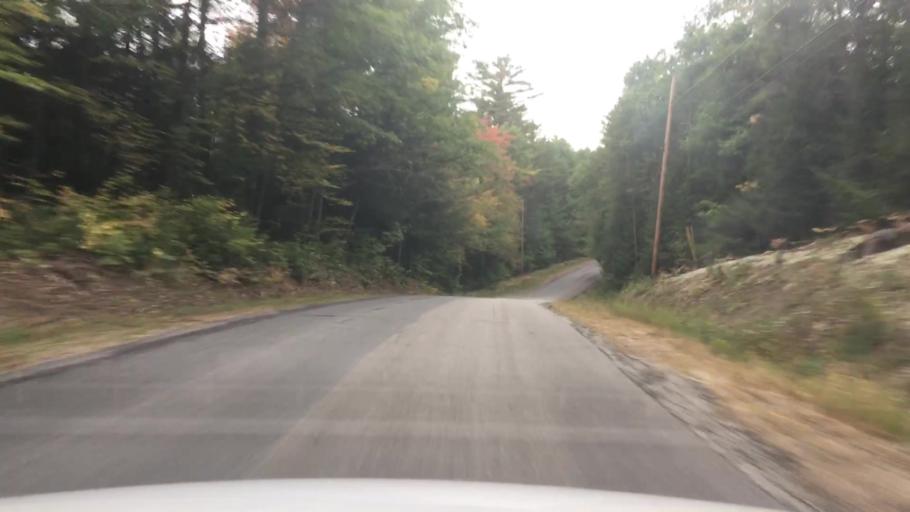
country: US
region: Maine
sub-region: Oxford County
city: Bethel
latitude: 44.4430
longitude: -70.7951
